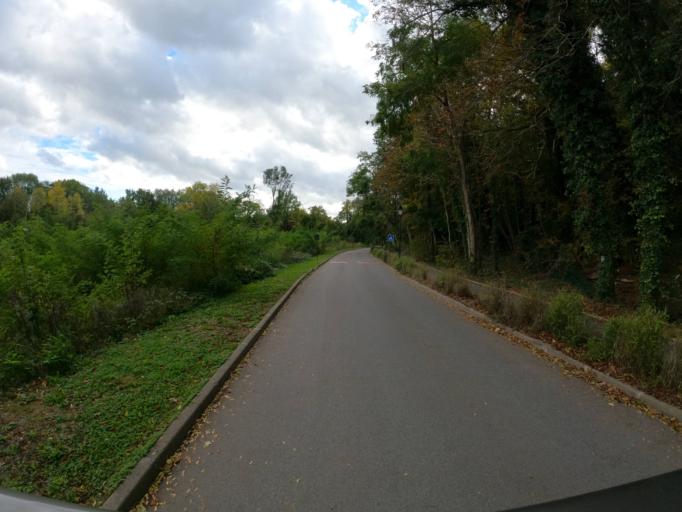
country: FR
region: Ile-de-France
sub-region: Departement de Seine-et-Marne
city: Coupvray
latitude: 48.9011
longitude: 2.7976
